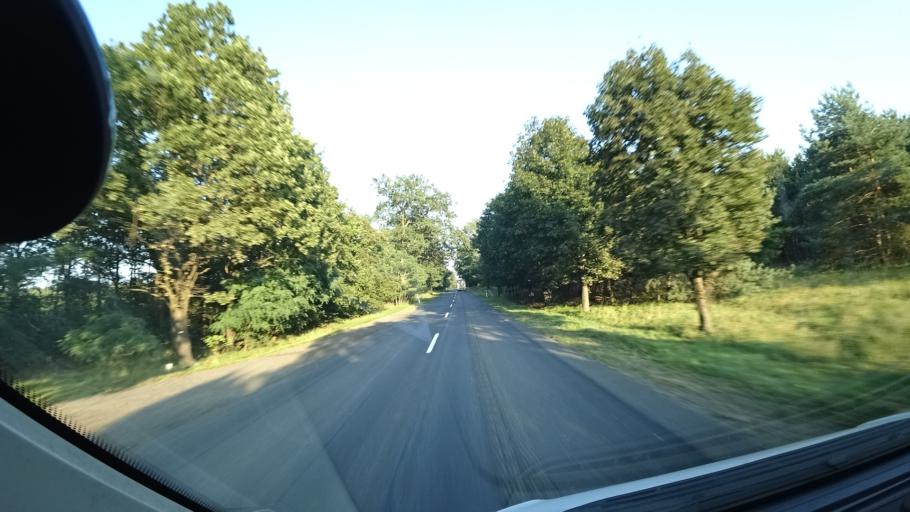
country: PL
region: Opole Voivodeship
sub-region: Powiat kedzierzynsko-kozielski
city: Dziergowice
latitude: 50.2810
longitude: 18.3341
